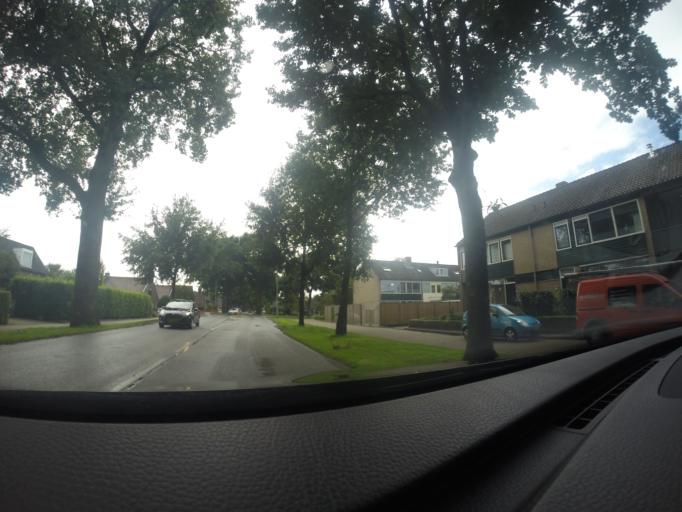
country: NL
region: Gelderland
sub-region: Gemeente Lochem
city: Lochem
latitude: 52.1556
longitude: 6.4096
